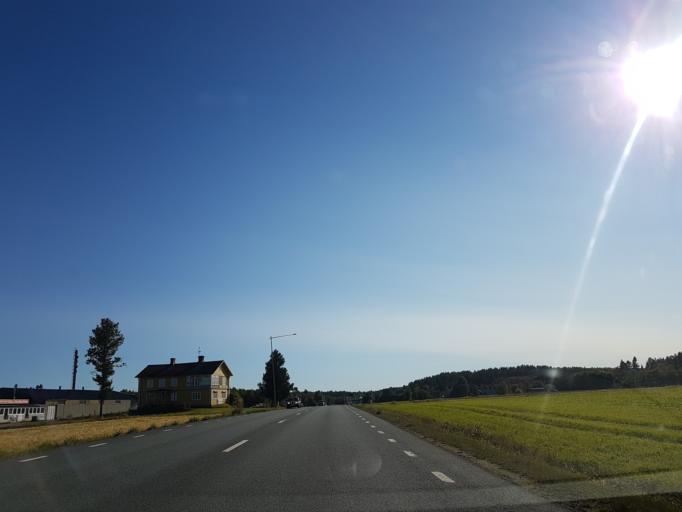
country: SE
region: Vaesterbotten
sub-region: Skelleftea Kommun
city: Burea
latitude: 64.3791
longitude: 21.3043
